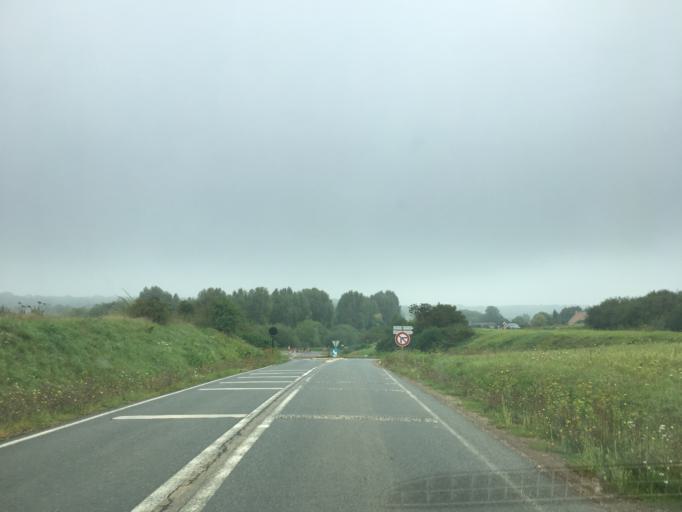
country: FR
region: Ile-de-France
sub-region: Departement de l'Essonne
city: Tigery
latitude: 48.6405
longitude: 2.5011
